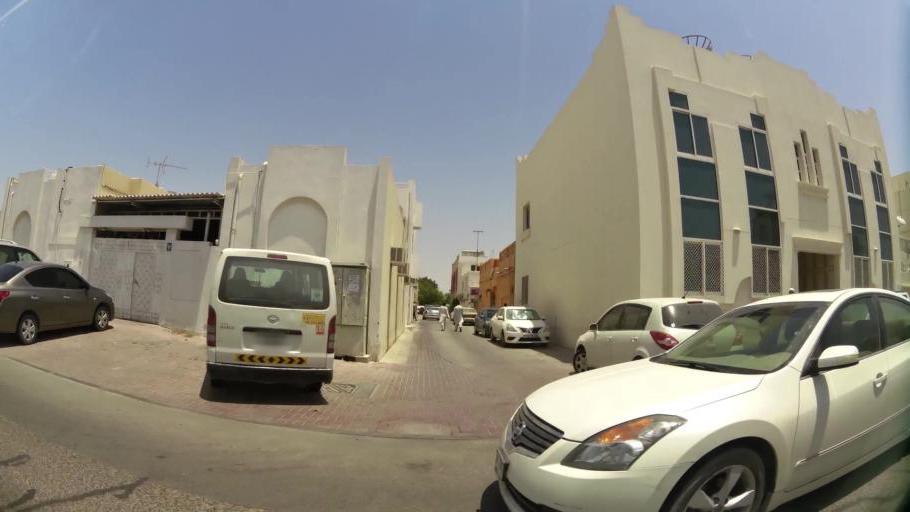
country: AE
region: Ash Shariqah
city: Sharjah
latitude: 25.2900
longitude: 55.3370
